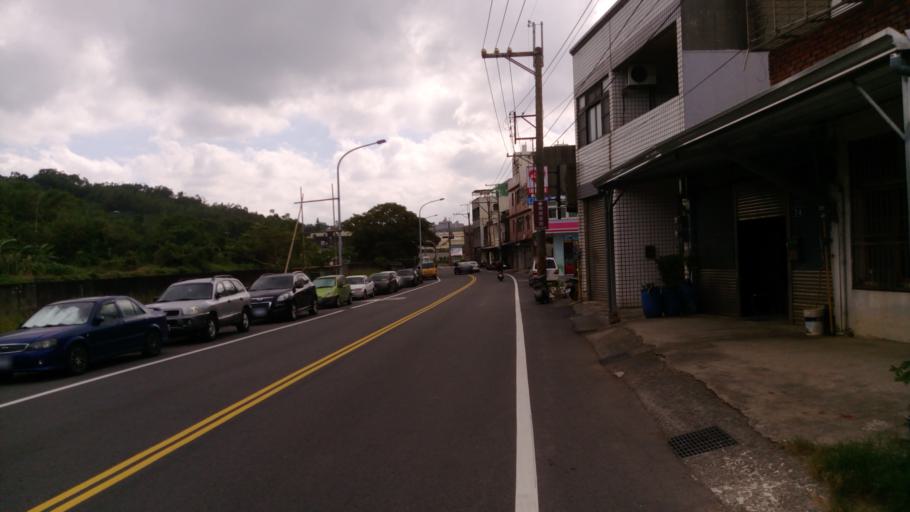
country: TW
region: Taiwan
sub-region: Hsinchu
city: Hsinchu
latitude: 24.7863
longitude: 120.9296
